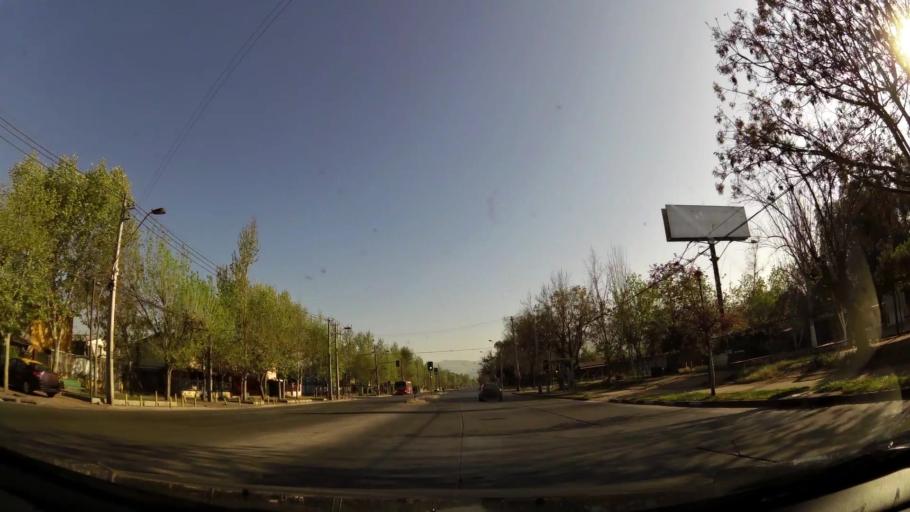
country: CL
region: Santiago Metropolitan
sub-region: Provincia de Santiago
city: Santiago
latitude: -33.3847
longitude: -70.6573
